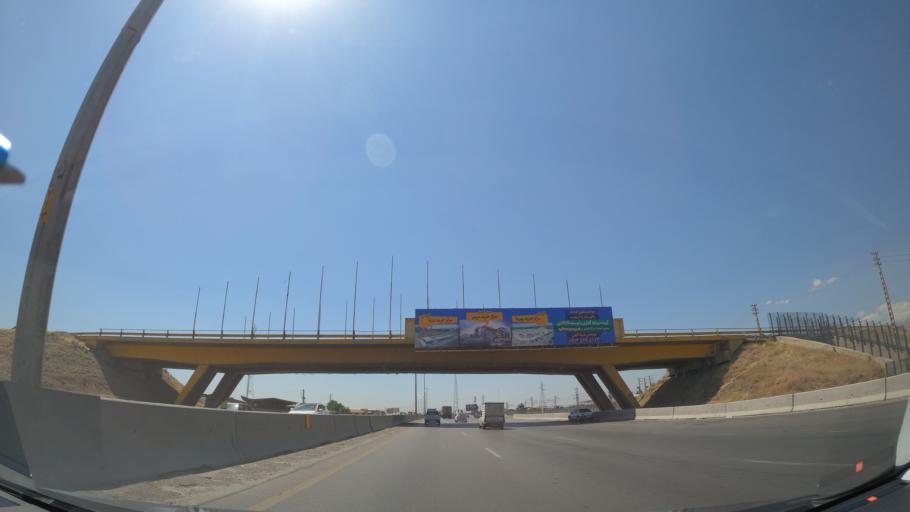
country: IR
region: Alborz
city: Hashtgerd
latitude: 35.9105
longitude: 50.8329
